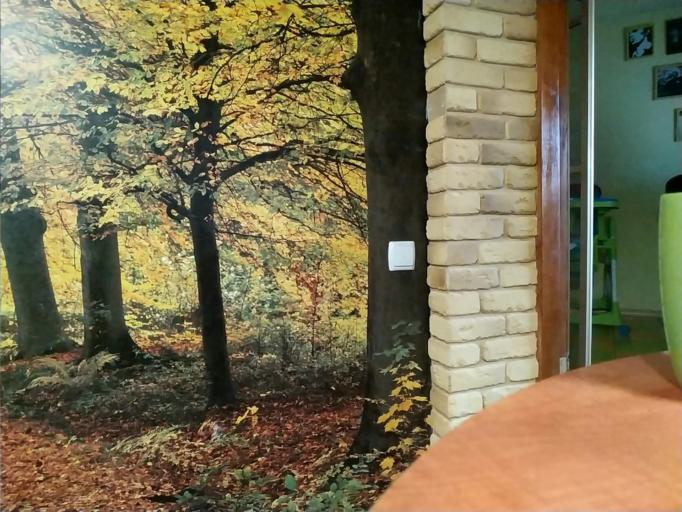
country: RU
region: Tverskaya
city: Staraya Toropa
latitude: 56.3514
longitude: 31.8123
